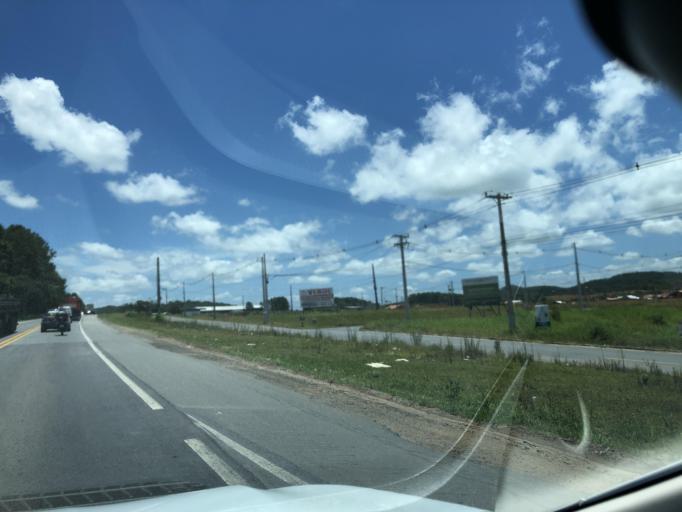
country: BR
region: Santa Catarina
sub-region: Joinville
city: Joinville
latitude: -26.4260
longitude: -48.7877
